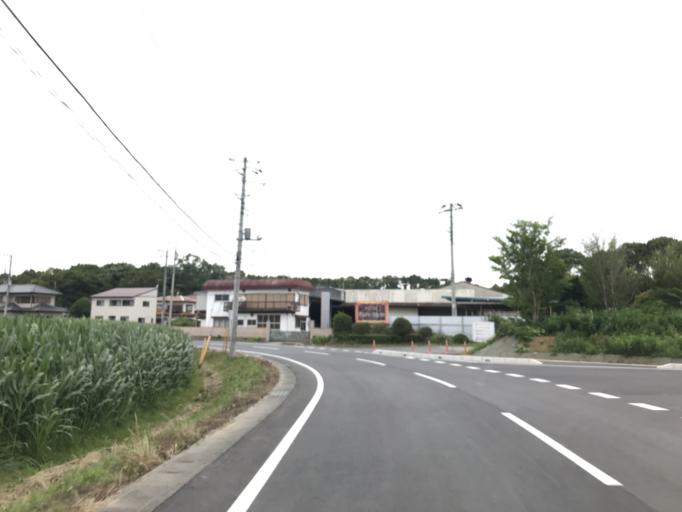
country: JP
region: Ibaraki
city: Ishioka
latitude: 36.2192
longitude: 140.2965
